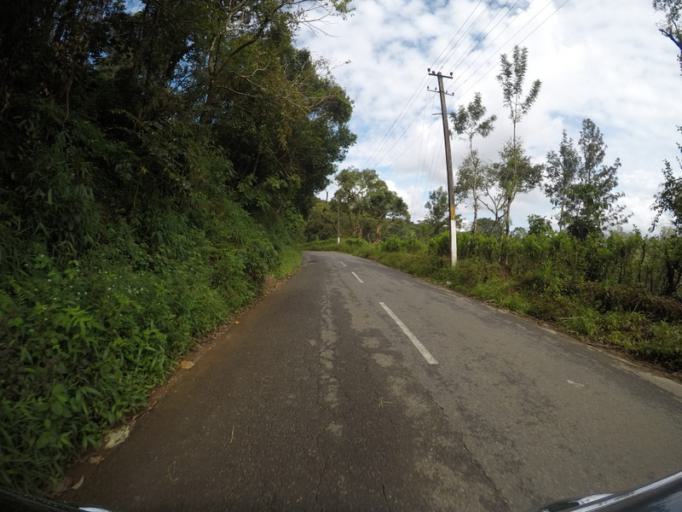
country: IN
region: Karnataka
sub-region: Kodagu
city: Madikeri
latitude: 12.4443
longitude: 75.7577
